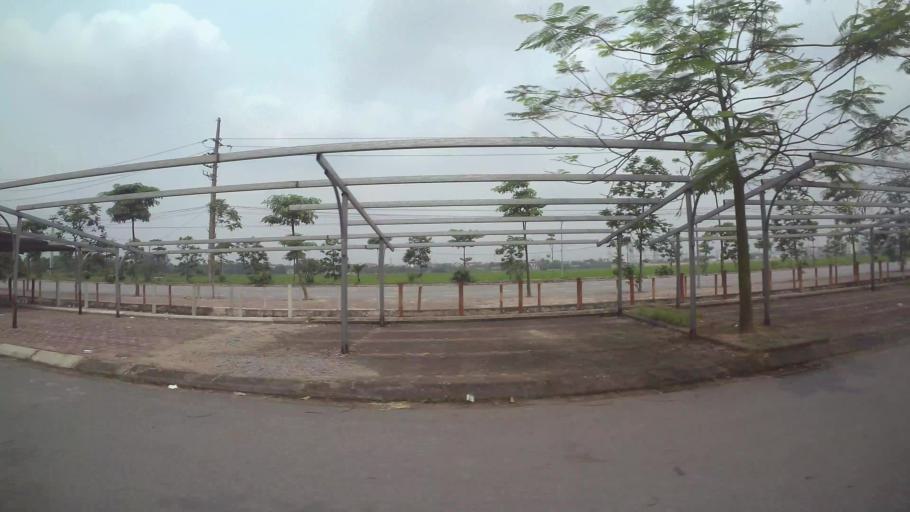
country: VN
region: Ha Noi
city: Trau Quy
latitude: 21.0689
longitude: 105.9105
